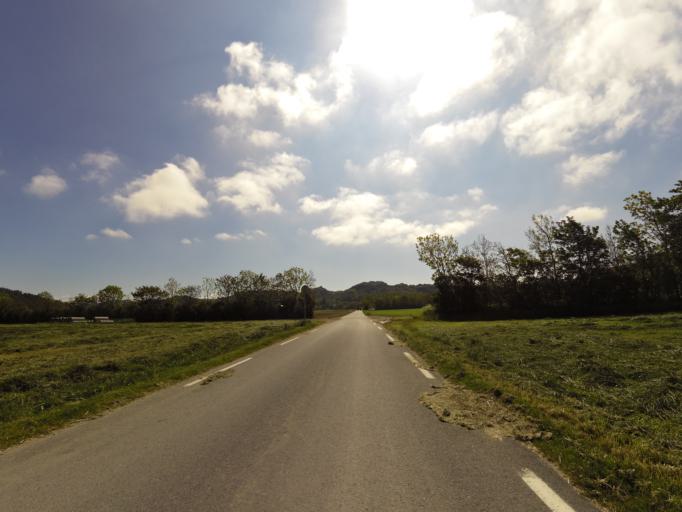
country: NO
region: Rogaland
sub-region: Ha
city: Vigrestad
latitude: 58.5193
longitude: 5.8133
